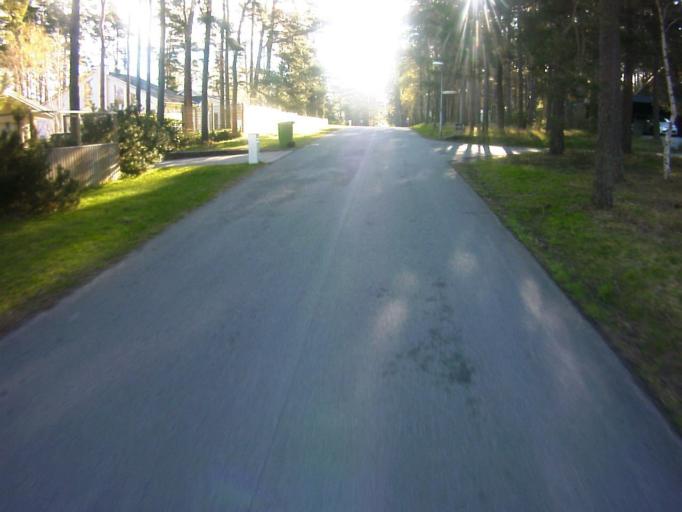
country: SE
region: Skane
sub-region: Kavlinge Kommun
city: Hofterup
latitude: 55.7988
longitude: 12.9749
